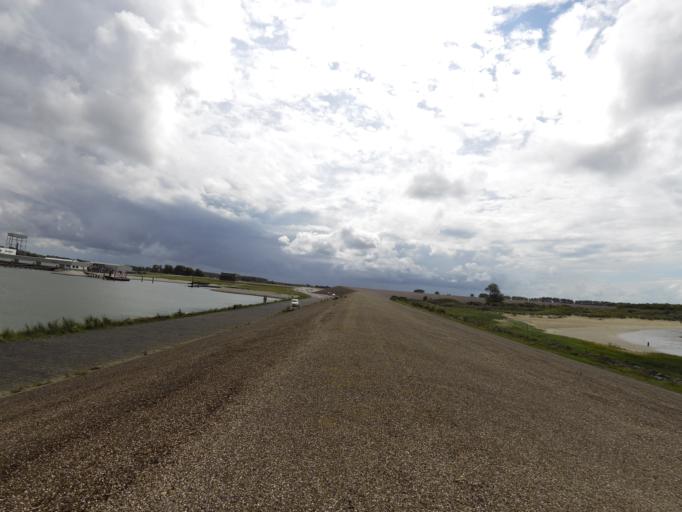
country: NL
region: South Holland
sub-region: Gemeente Goeree-Overflakkee
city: Goedereede
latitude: 51.8293
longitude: 4.0301
